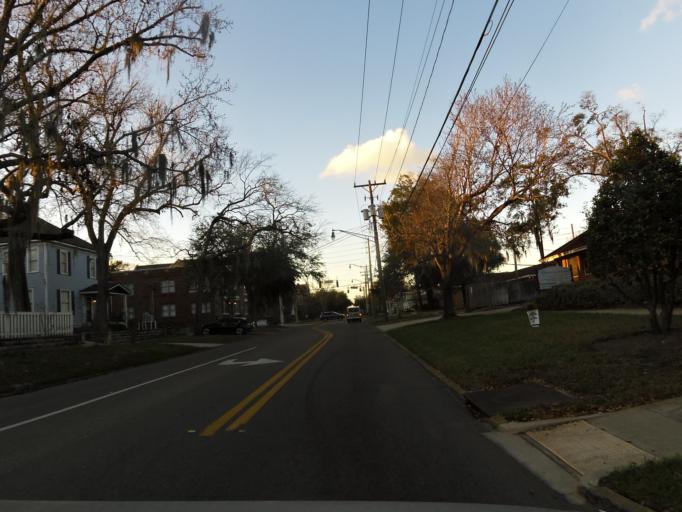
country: US
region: Florida
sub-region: Duval County
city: Jacksonville
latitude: 30.3114
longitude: -81.6883
